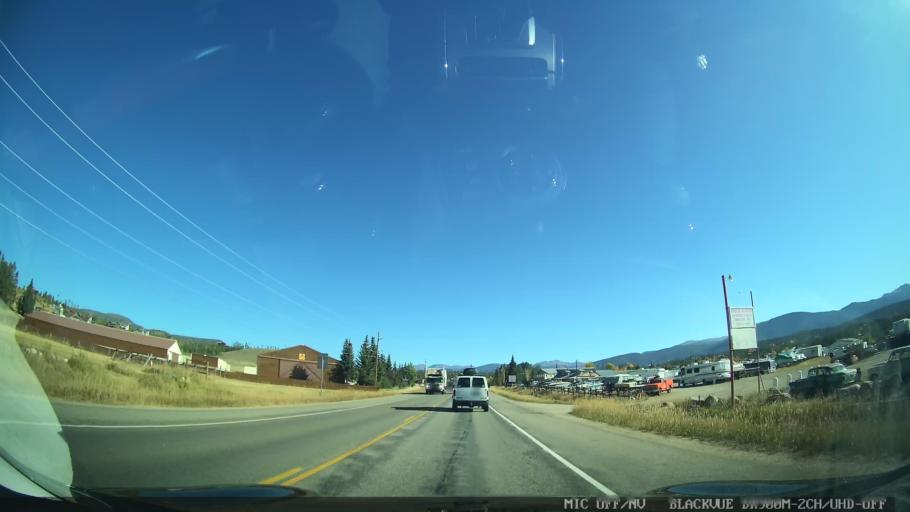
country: US
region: Colorado
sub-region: Grand County
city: Granby
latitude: 40.1900
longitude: -105.8814
